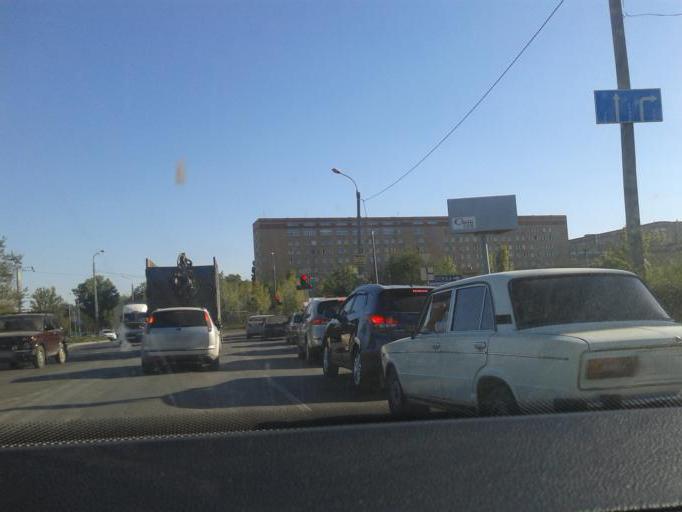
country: RU
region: Volgograd
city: Volgograd
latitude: 48.7647
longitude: 44.5164
